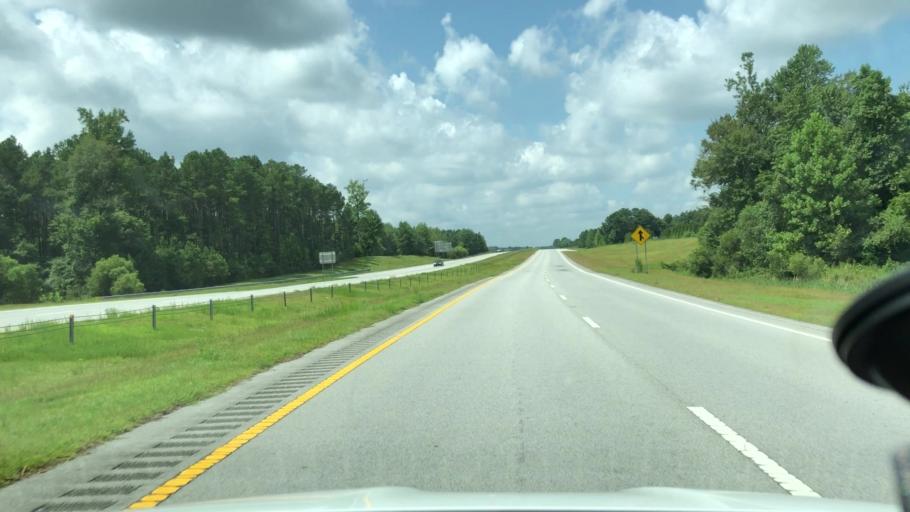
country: US
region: North Carolina
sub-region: Beaufort County
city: Washington
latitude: 35.5060
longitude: -77.0917
